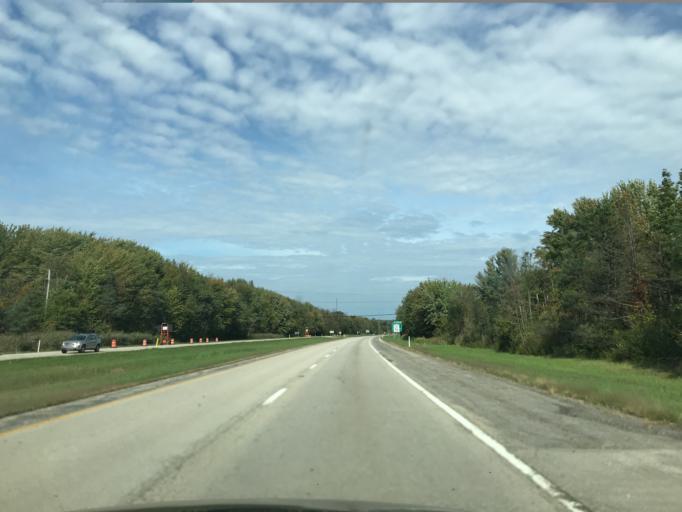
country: US
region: Ohio
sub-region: Ashtabula County
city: Ashtabula
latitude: 41.8139
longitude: -80.7616
